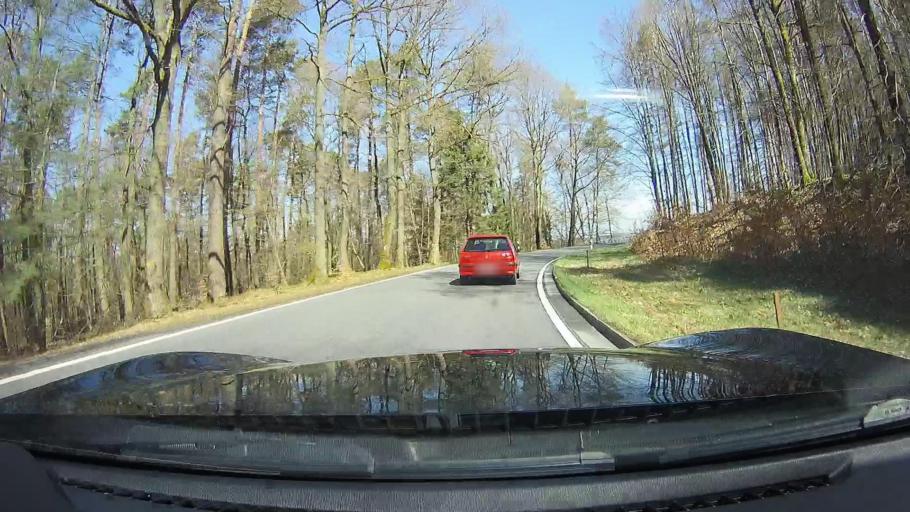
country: DE
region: Hesse
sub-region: Regierungsbezirk Darmstadt
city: Beerfelden
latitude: 49.5432
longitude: 8.9381
